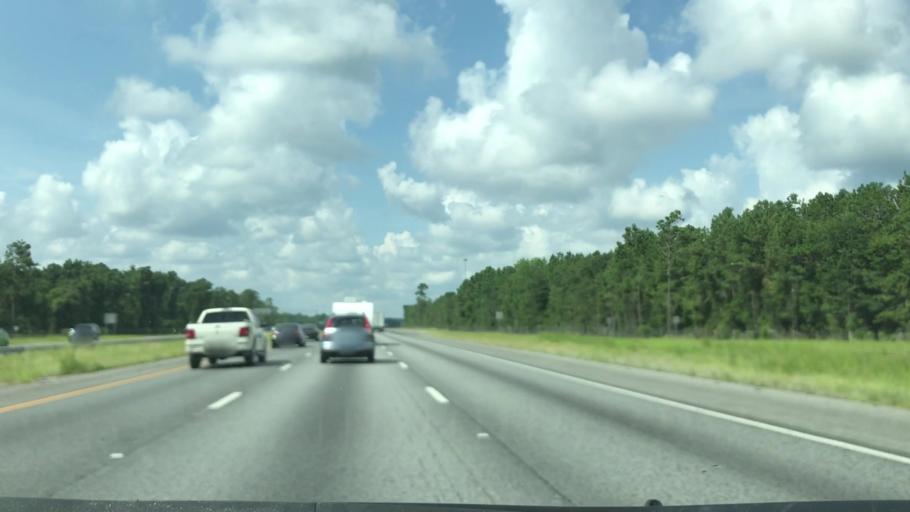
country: US
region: Georgia
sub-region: Glynn County
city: Brunswick
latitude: 31.0998
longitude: -81.6000
